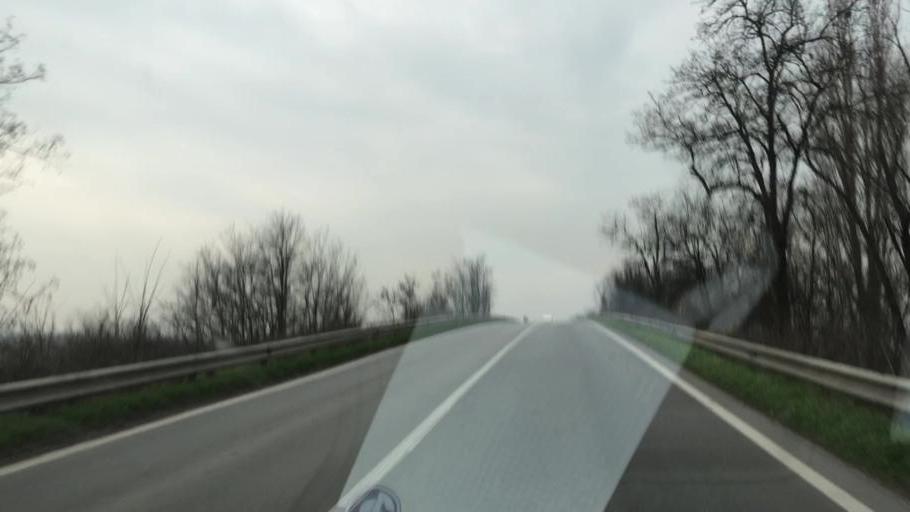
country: IT
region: Lombardy
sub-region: Provincia di Mantova
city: Asola
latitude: 45.2271
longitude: 10.4037
